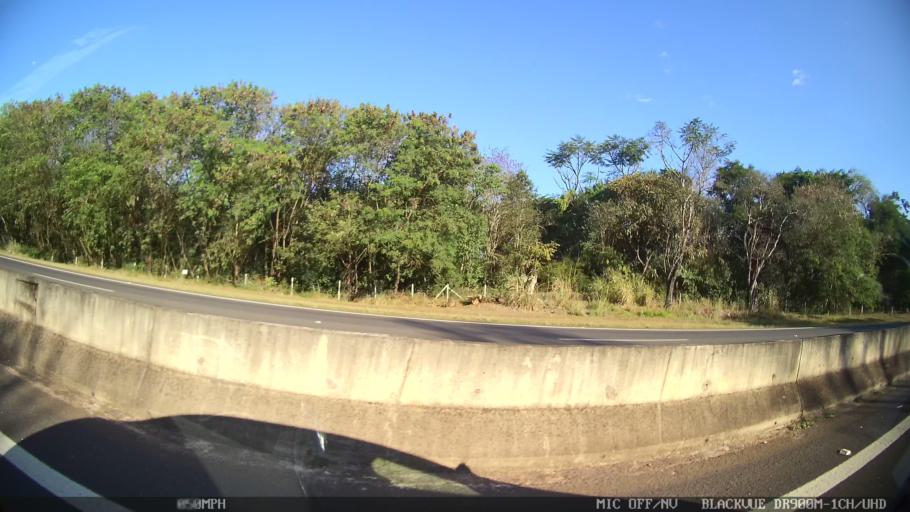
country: BR
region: Sao Paulo
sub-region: Piracicaba
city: Piracicaba
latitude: -22.7015
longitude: -47.6433
